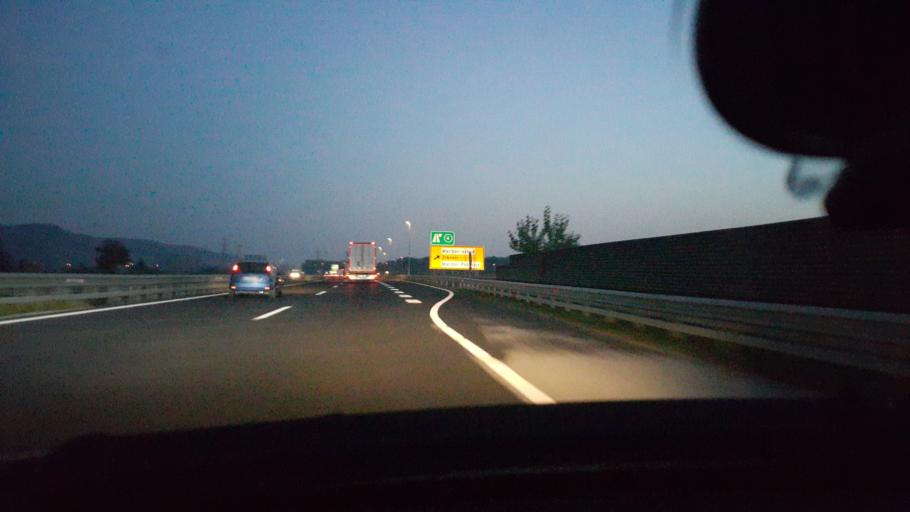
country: SI
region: Miklavz na Dravskem Polju
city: Miklavz na Dravskem Polju
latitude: 46.5488
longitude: 15.6924
